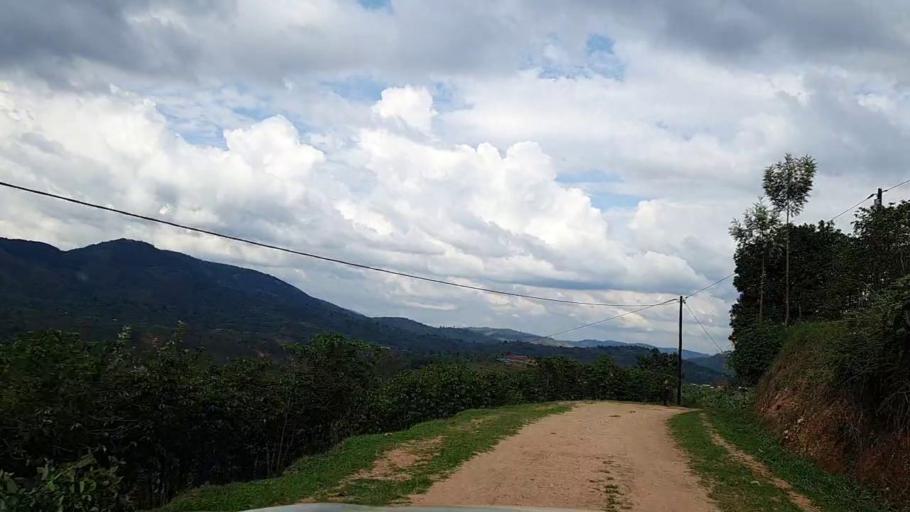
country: RW
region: Southern Province
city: Gikongoro
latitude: -2.4247
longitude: 29.6423
